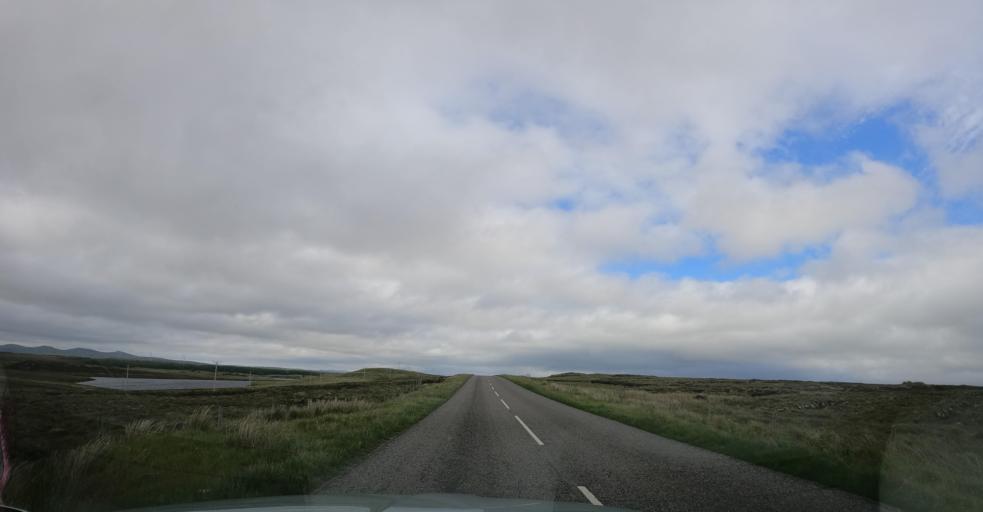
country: GB
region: Scotland
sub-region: Eilean Siar
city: Stornoway
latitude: 58.1645
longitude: -6.4886
